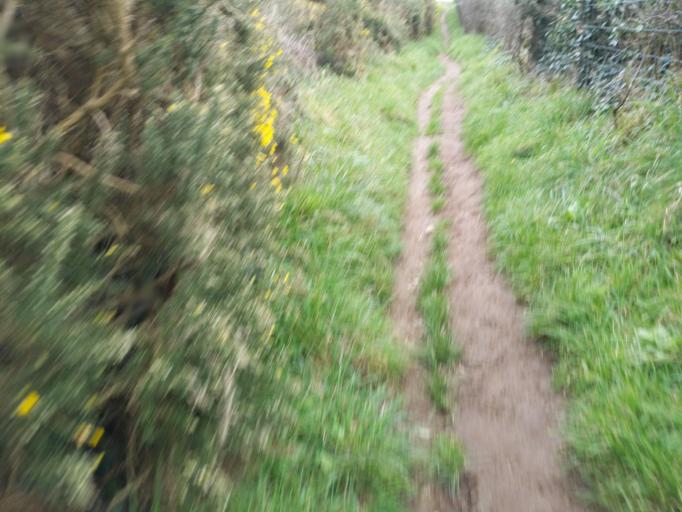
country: GB
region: England
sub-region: Devon
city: Salcombe
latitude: 50.2103
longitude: -3.7295
